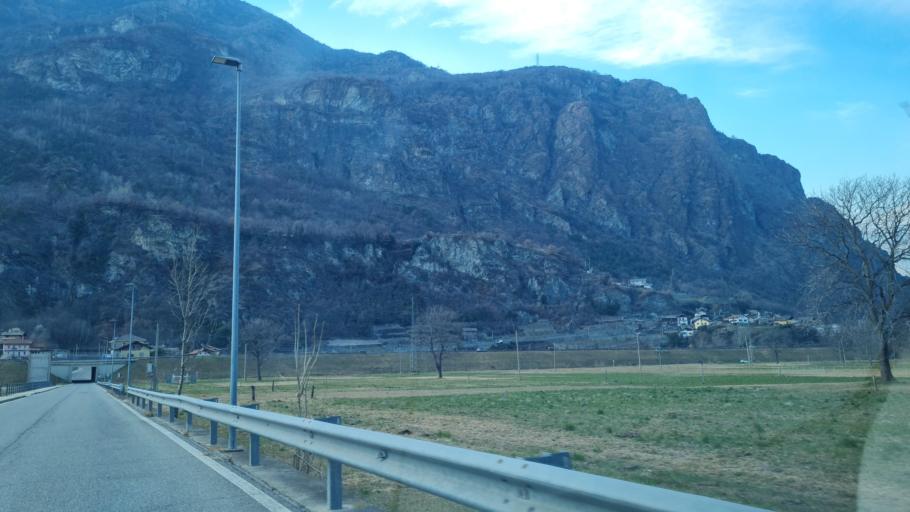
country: IT
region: Aosta Valley
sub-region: Valle d'Aosta
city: Montjovet
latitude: 45.7046
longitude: 7.6714
